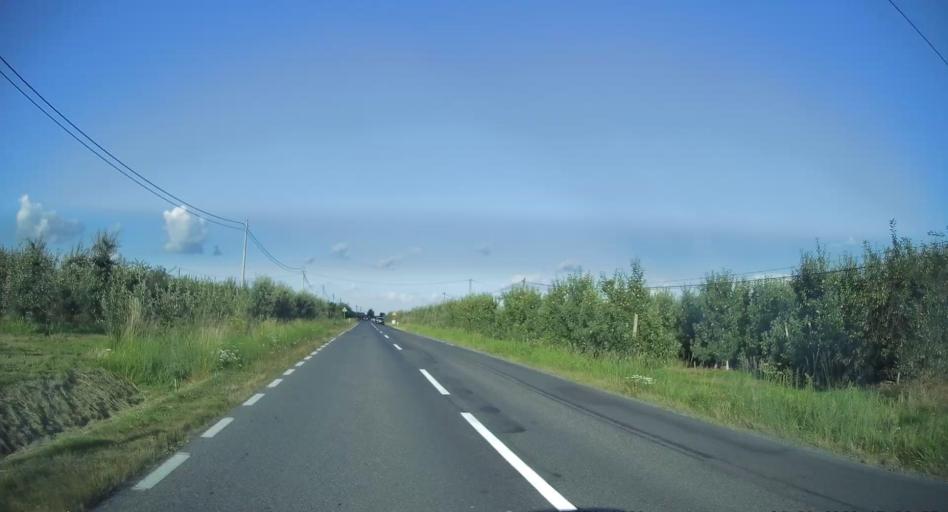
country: PL
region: Masovian Voivodeship
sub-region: Powiat grojecki
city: Bledow
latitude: 51.8031
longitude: 20.6390
